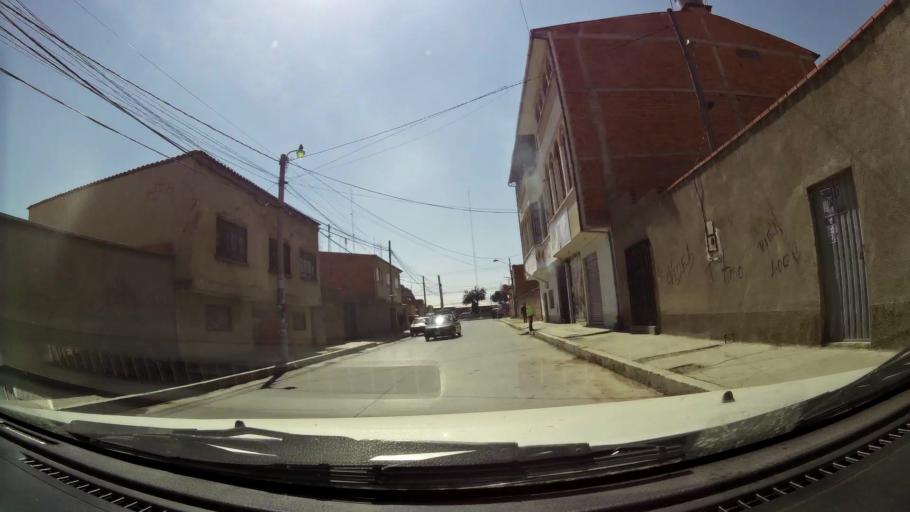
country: BO
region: La Paz
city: La Paz
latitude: -16.5259
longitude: -68.1480
